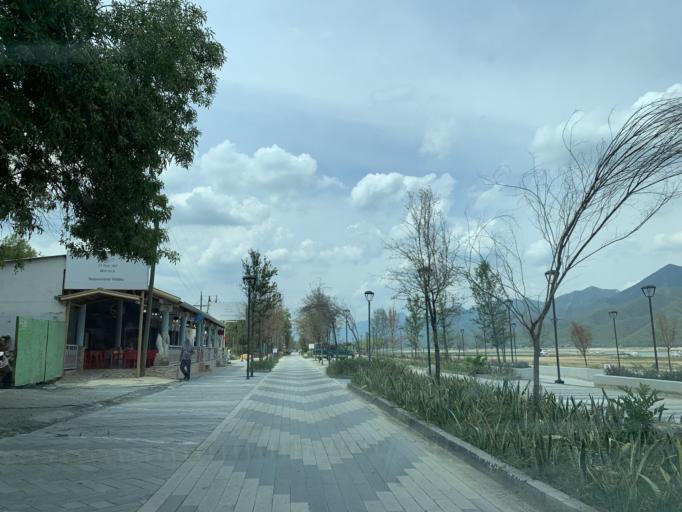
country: MX
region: Nuevo Leon
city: Santiago
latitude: 25.4117
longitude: -100.1381
